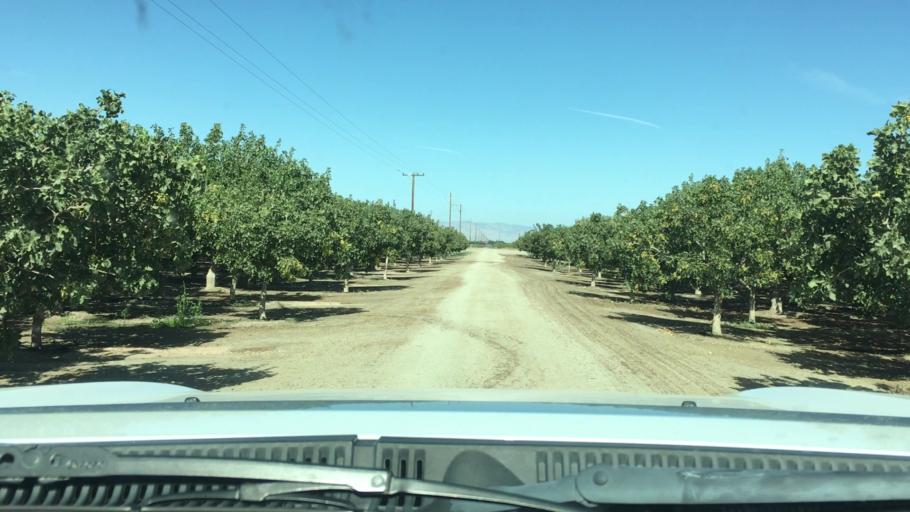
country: US
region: California
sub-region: Kern County
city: Buttonwillow
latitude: 35.3694
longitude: -119.3965
